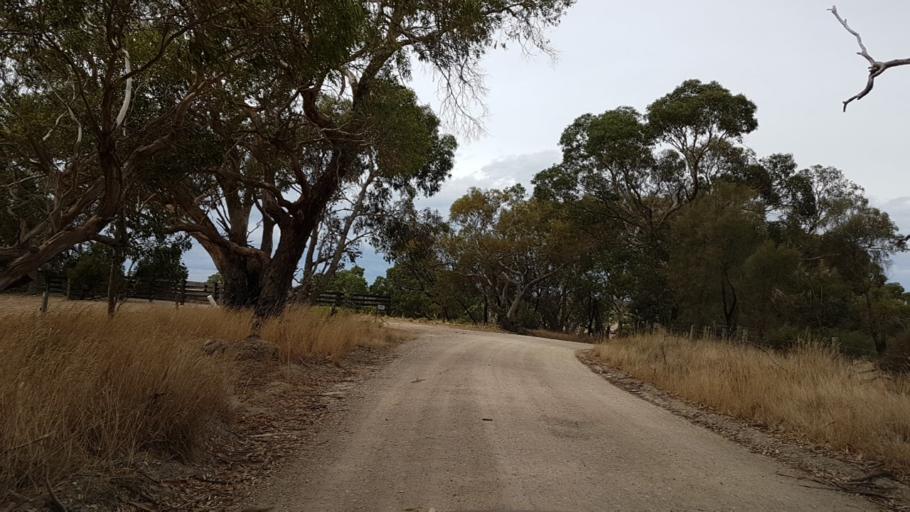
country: AU
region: South Australia
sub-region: Adelaide Hills
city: Birdwood
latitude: -34.7620
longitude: 139.0026
